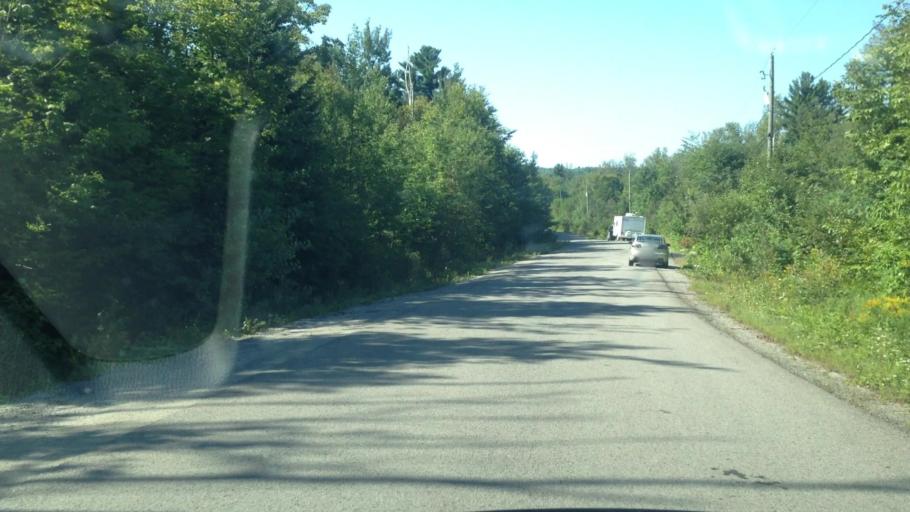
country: CA
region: Quebec
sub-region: Laurentides
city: Prevost
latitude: 45.8677
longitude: -74.0162
